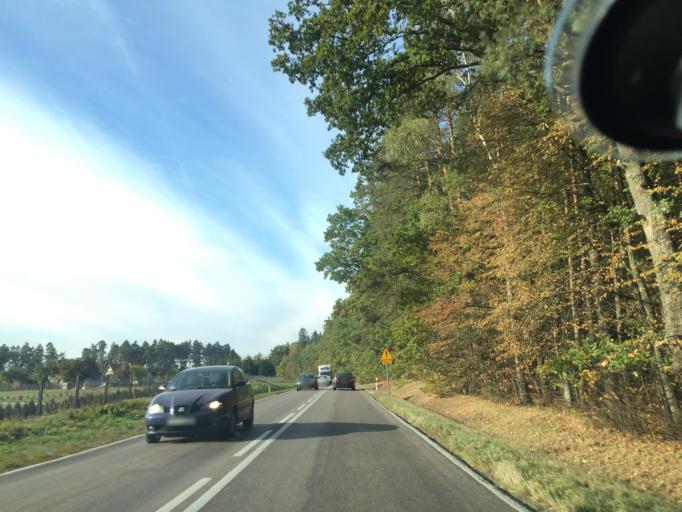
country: PL
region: Warmian-Masurian Voivodeship
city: Dobre Miasto
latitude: 54.0336
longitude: 20.4221
